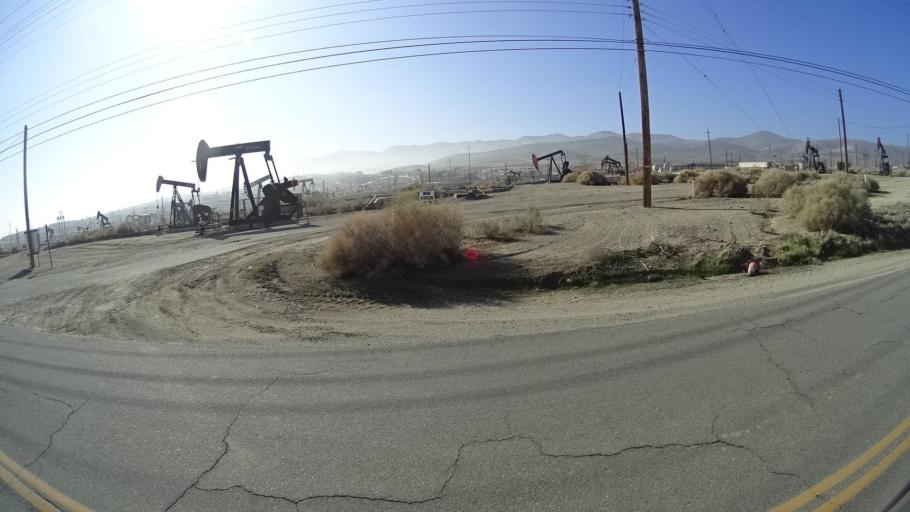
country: US
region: California
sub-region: Kern County
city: Taft Heights
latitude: 35.2233
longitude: -119.6206
